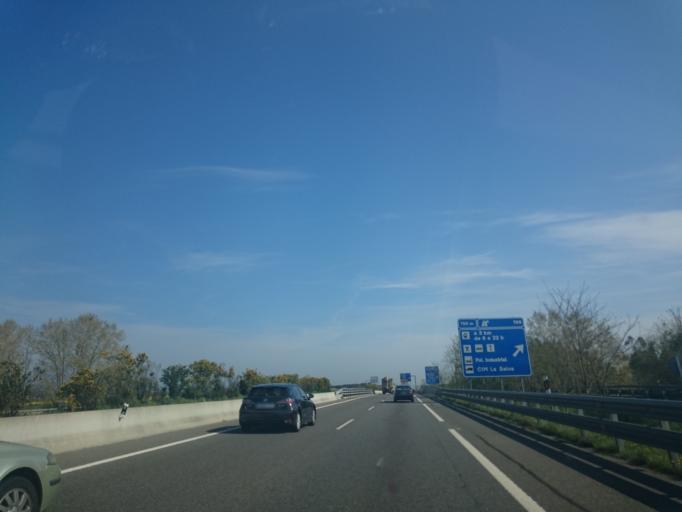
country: ES
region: Catalonia
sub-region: Provincia de Girona
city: Riudellots de la Selva
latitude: 41.8776
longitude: 2.7800
